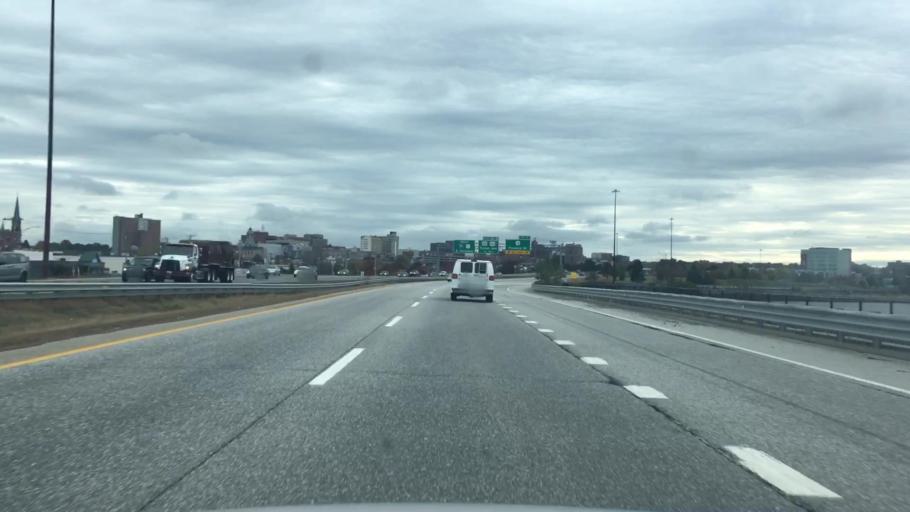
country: US
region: Maine
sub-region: Cumberland County
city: Portland
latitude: 43.6706
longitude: -70.2587
